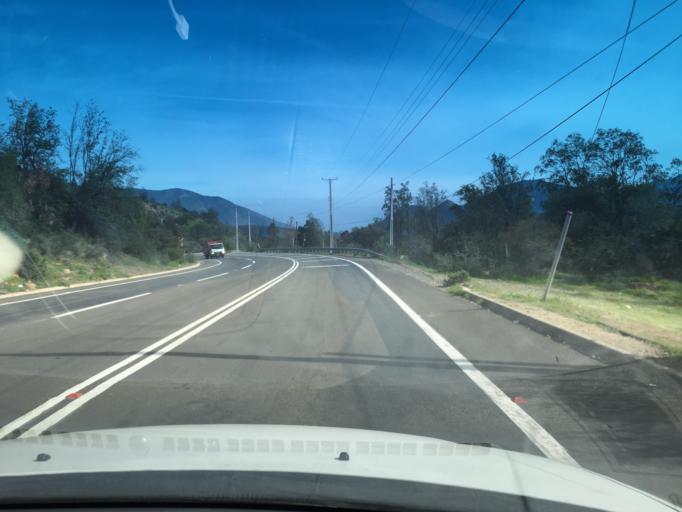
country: CL
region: Valparaiso
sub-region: Provincia de San Felipe
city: Llaillay
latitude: -33.0633
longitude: -71.0286
